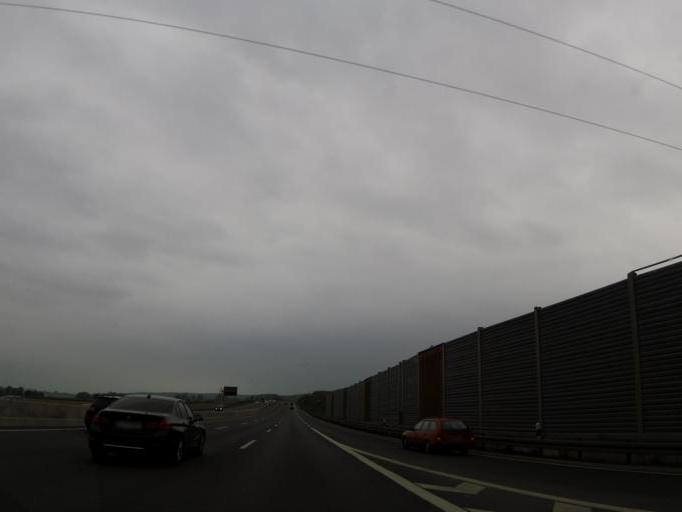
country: DE
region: Lower Saxony
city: Norten-Hardenberg
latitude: 51.6275
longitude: 9.9172
